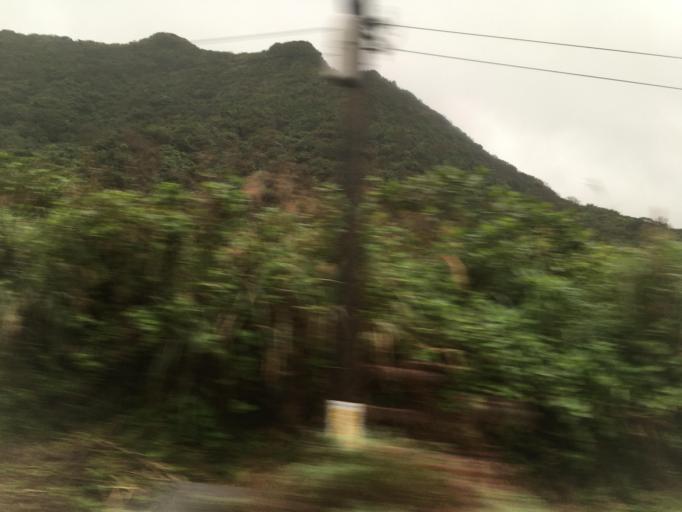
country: TW
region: Taiwan
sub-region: Keelung
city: Keelung
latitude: 25.1127
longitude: 121.9131
